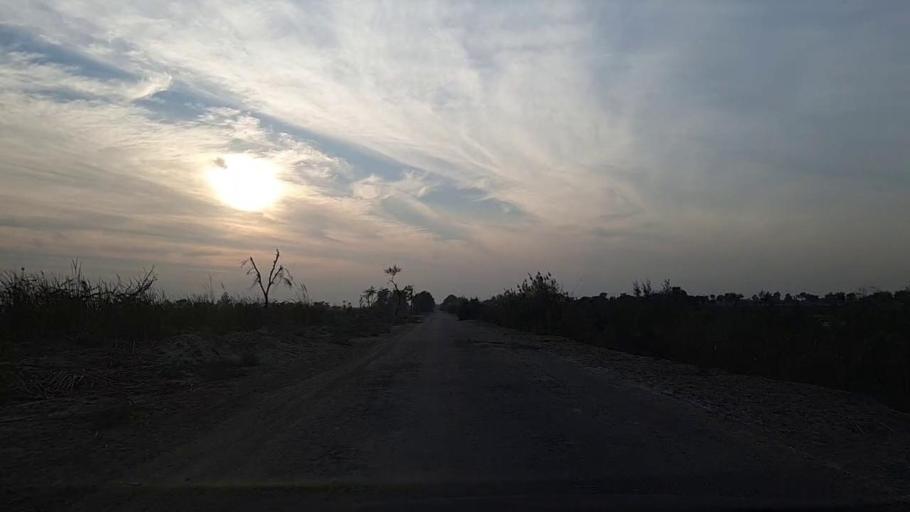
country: PK
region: Sindh
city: Daur
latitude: 26.3990
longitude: 68.4598
